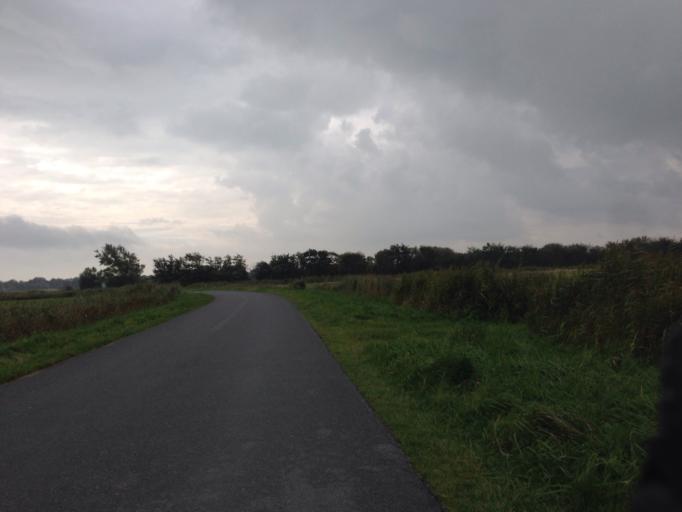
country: DE
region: Schleswig-Holstein
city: Oevenum
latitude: 54.7185
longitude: 8.5368
